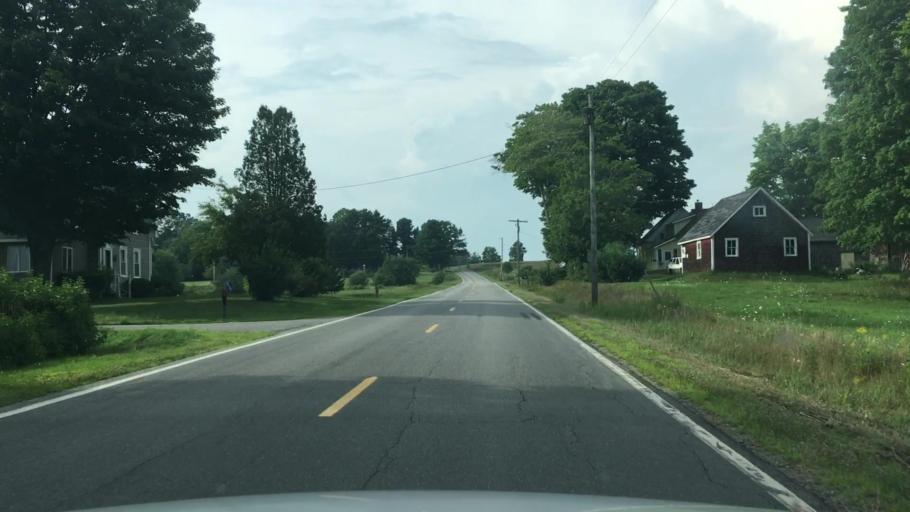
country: US
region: Maine
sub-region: Knox County
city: Washington
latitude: 44.2124
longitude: -69.3834
